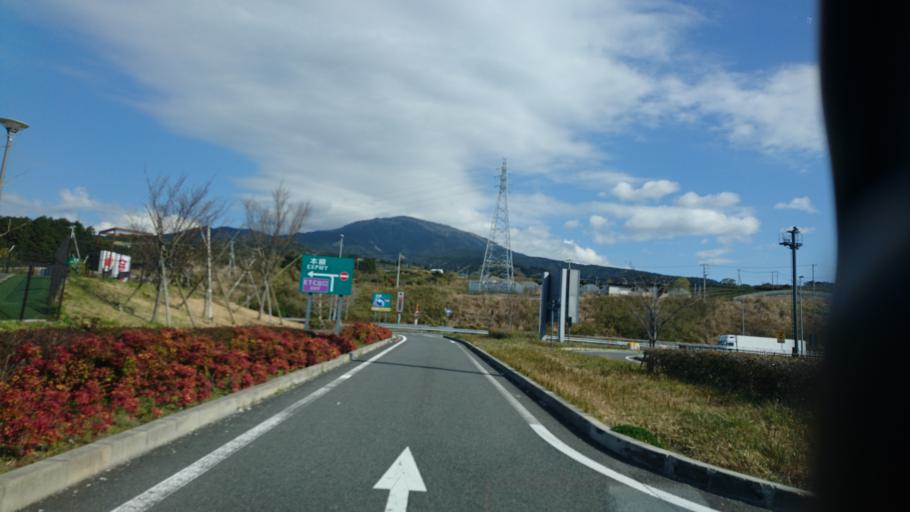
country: JP
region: Shizuoka
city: Numazu
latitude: 35.1524
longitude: 138.8119
